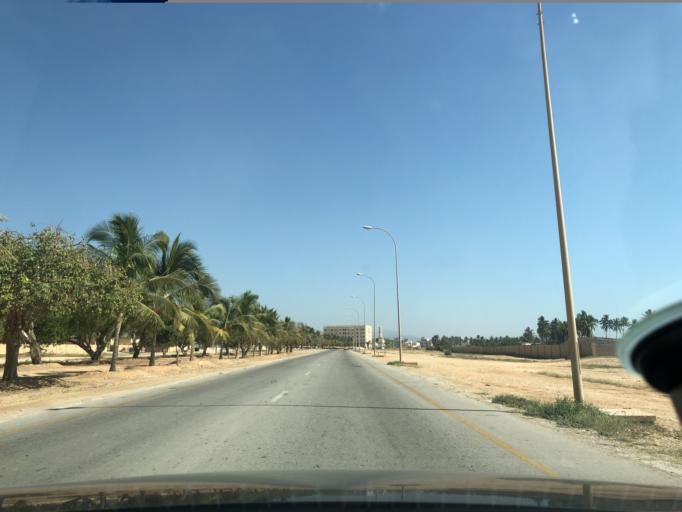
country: OM
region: Zufar
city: Salalah
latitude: 17.0389
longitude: 54.3813
